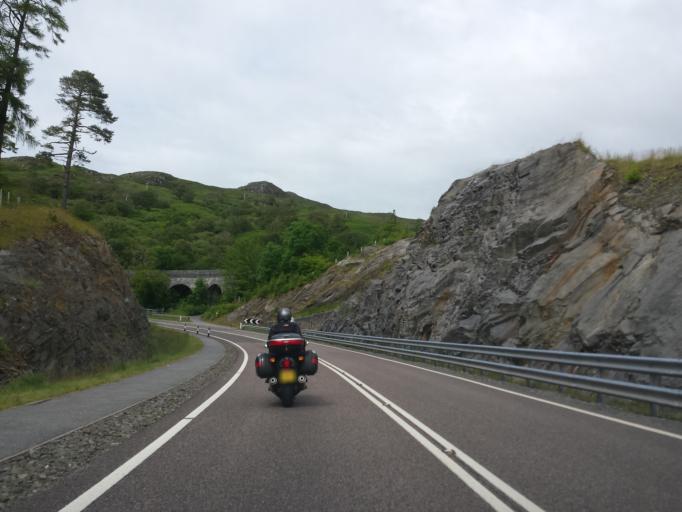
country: GB
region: Scotland
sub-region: Argyll and Bute
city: Isle Of Mull
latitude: 56.9109
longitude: -5.8218
